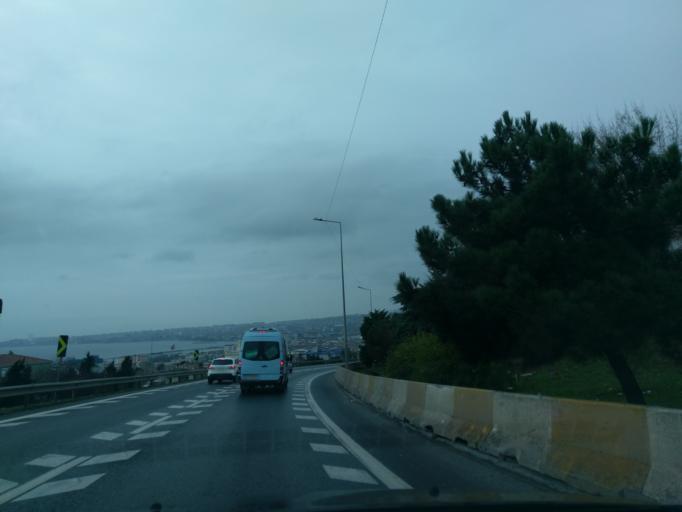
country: TR
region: Istanbul
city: Bueyuekcekmece
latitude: 41.0241
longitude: 28.5978
